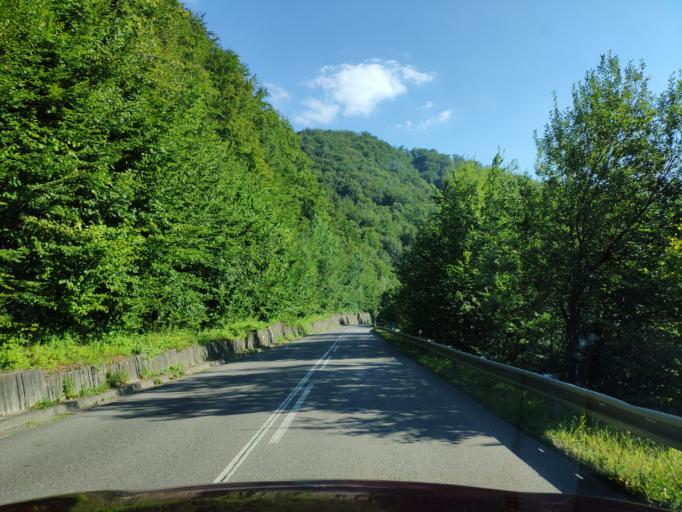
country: SK
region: Presovsky
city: Snina
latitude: 49.0418
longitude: 22.2612
